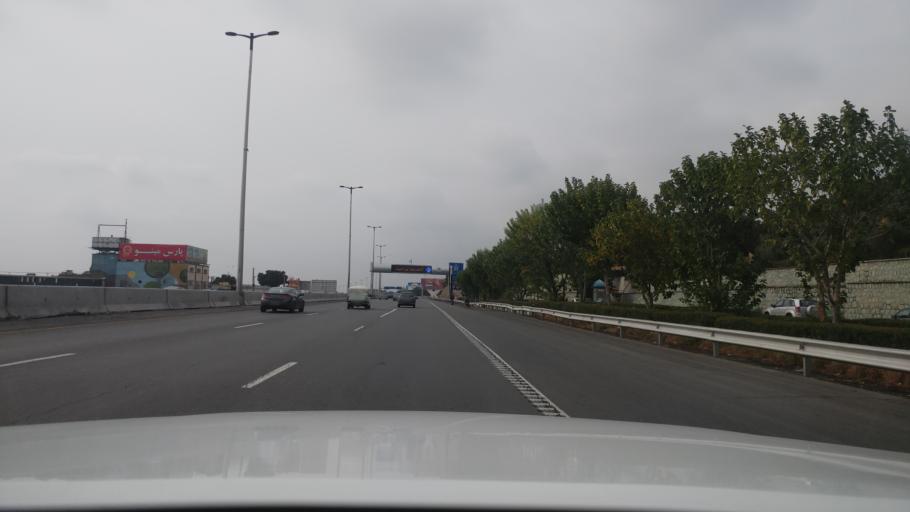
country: IR
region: Tehran
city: Shahr-e Qods
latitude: 35.7169
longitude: 51.2369
